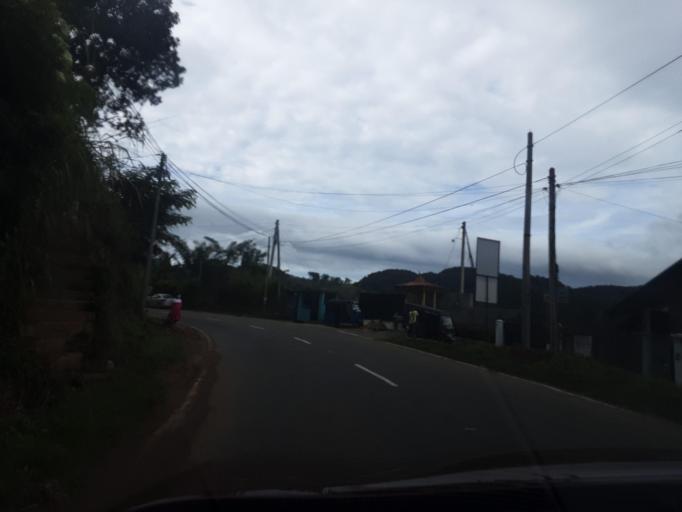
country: LK
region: Uva
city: Haputale
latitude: 6.8429
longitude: 80.9739
